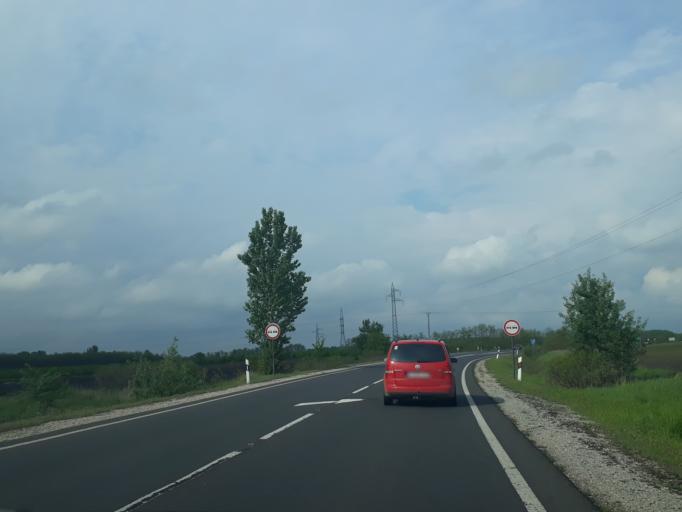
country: HU
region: Szabolcs-Szatmar-Bereg
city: Nyirbogdany
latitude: 48.0645
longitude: 21.9299
